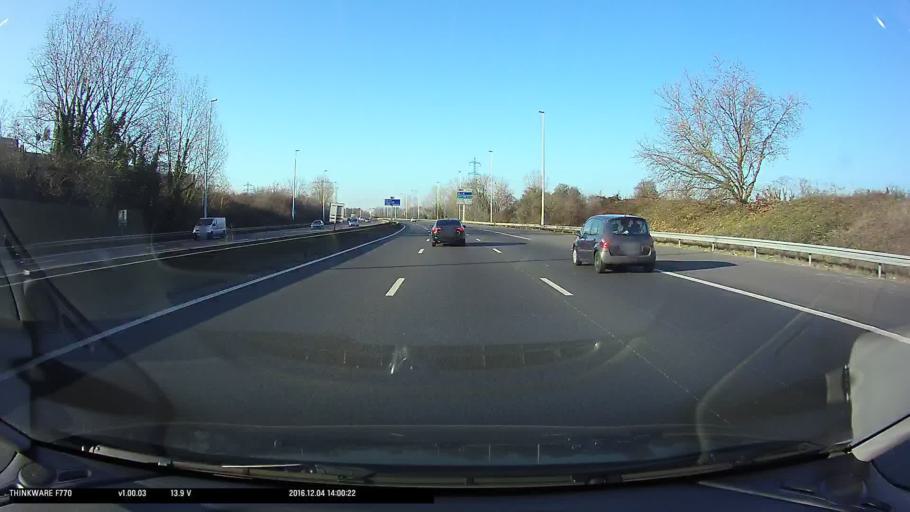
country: FR
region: Ile-de-France
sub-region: Departement du Val-d'Oise
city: Saint-Ouen-l'Aumone
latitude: 49.0288
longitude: 2.1274
